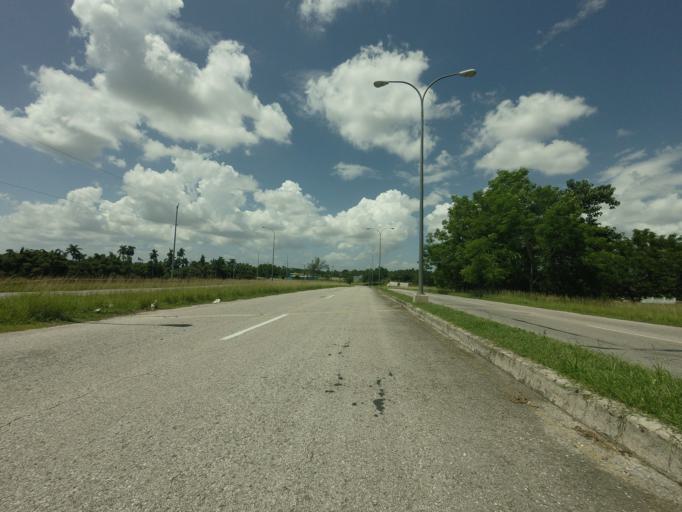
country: CU
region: La Habana
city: Arroyo Naranjo
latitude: 23.0346
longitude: -82.3513
